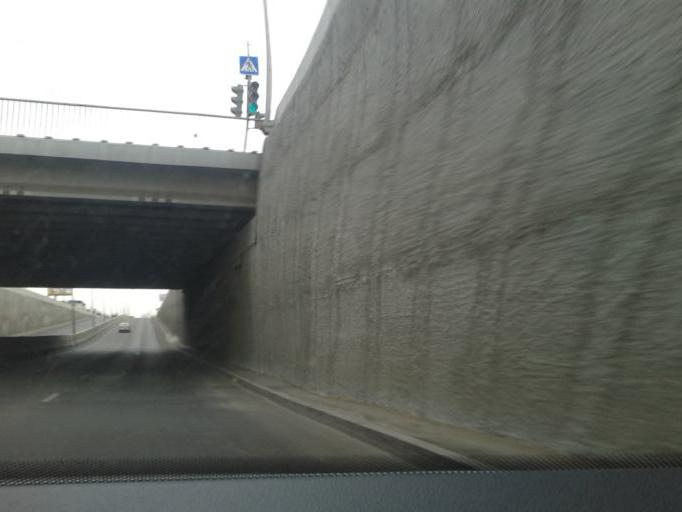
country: RU
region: Volgograd
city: Volgograd
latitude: 48.6359
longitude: 44.4301
